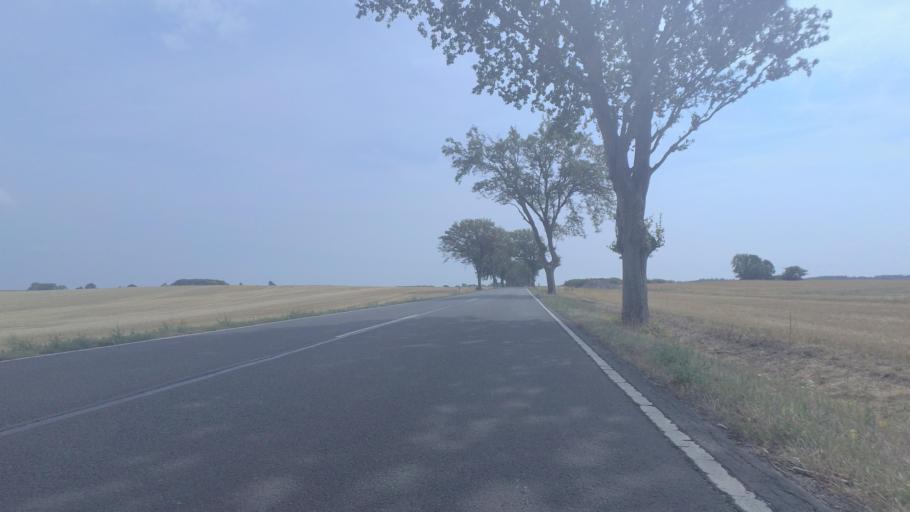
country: DE
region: Mecklenburg-Vorpommern
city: Samtens
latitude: 54.3448
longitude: 13.3067
